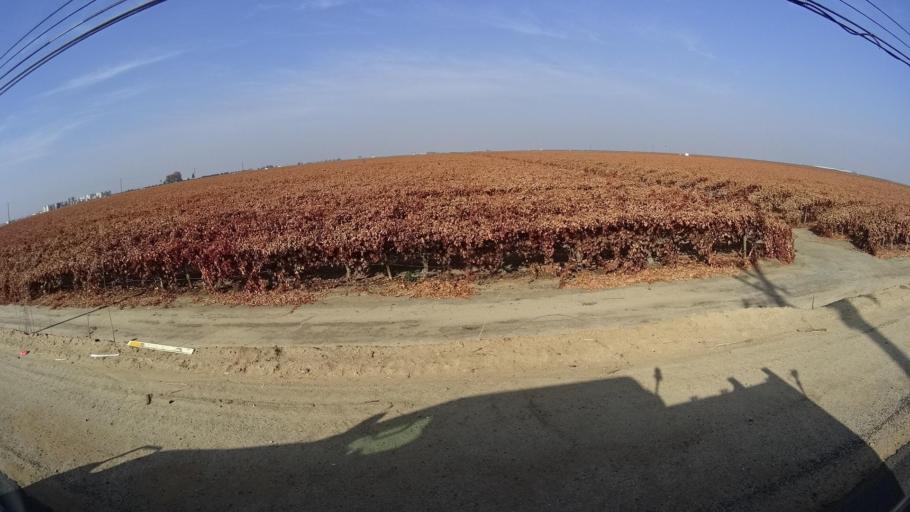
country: US
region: California
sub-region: Kern County
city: Delano
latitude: 35.7759
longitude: -119.1811
